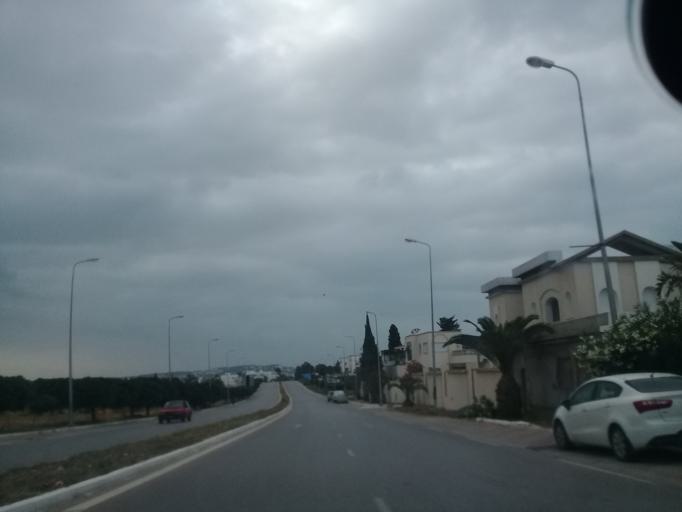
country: TN
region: Tunis
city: Sidi Bou Said
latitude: 36.8676
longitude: 10.3357
